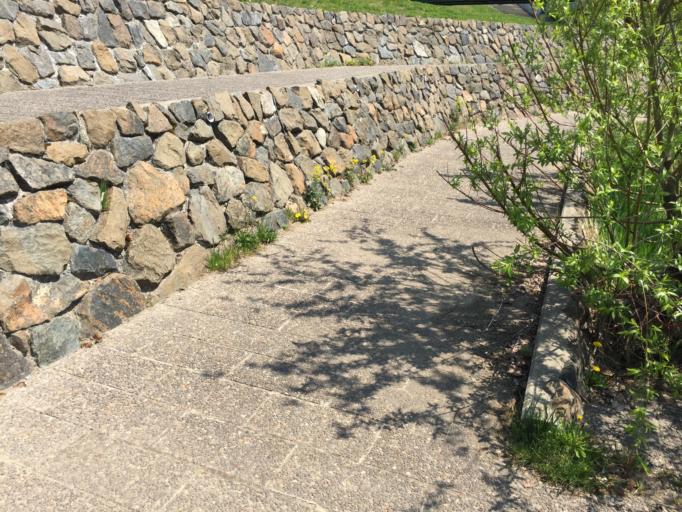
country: JP
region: Hokkaido
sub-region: Asahikawa-shi
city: Asahikawa
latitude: 43.7558
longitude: 142.3661
